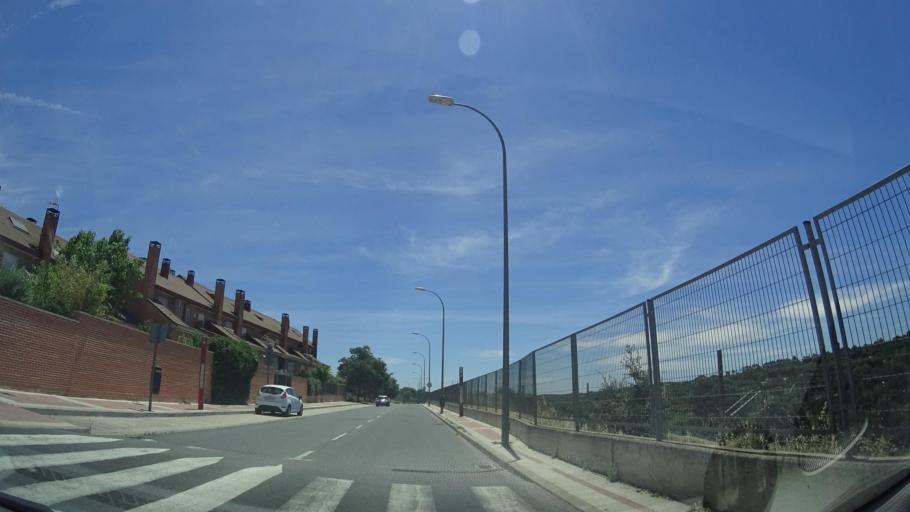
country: ES
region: Madrid
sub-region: Provincia de Madrid
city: Collado-Villalba
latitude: 40.6223
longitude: -3.9969
